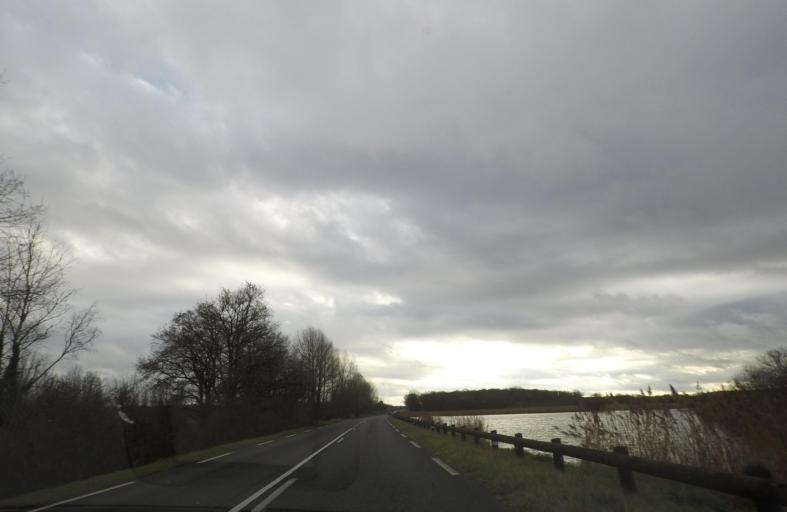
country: FR
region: Centre
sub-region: Departement du Loir-et-Cher
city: Soings-en-Sologne
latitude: 47.4365
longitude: 1.5565
